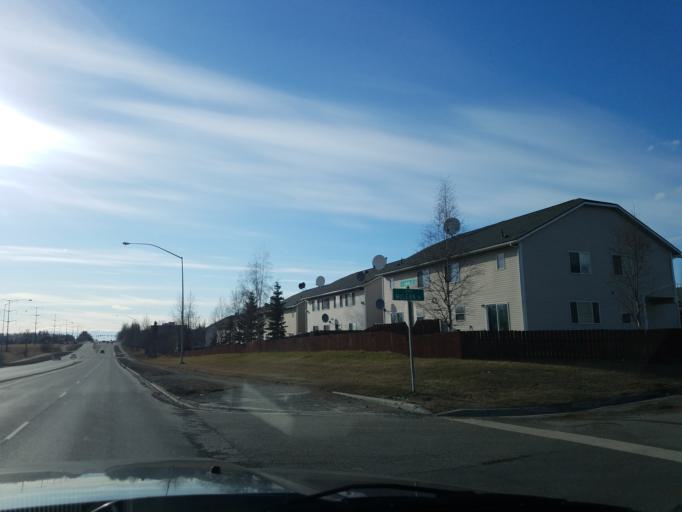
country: US
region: Alaska
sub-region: Anchorage Municipality
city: Anchorage
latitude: 61.1808
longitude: -149.7672
